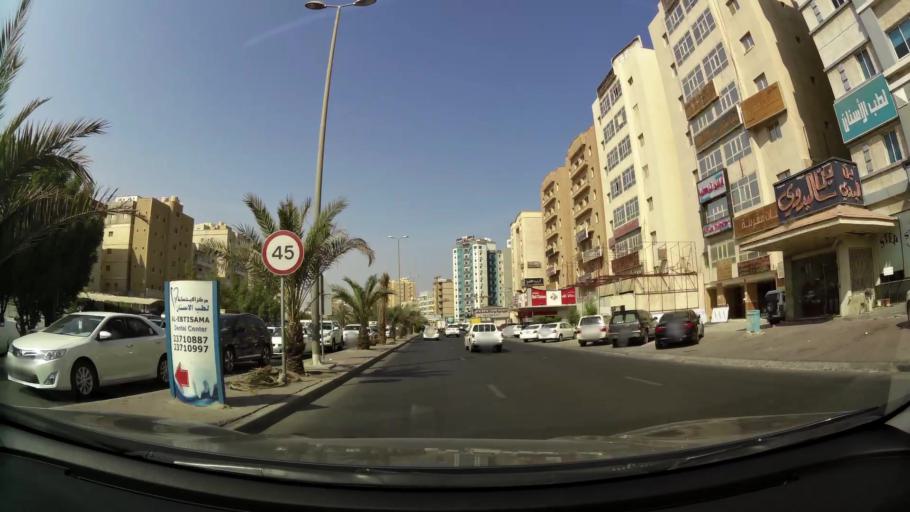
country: KW
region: Al Ahmadi
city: Al Manqaf
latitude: 29.0925
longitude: 48.1301
